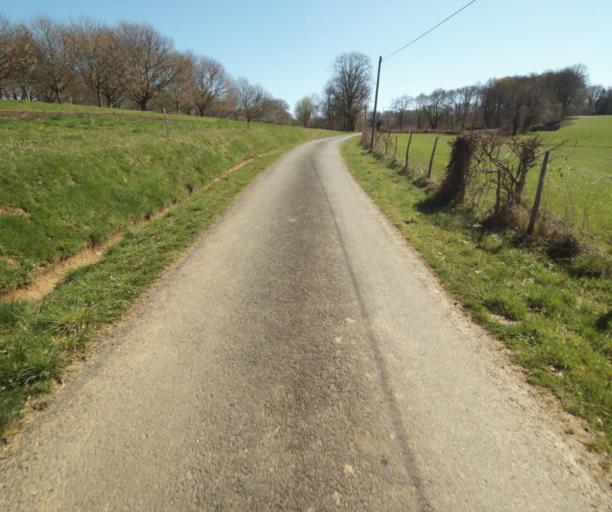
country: FR
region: Limousin
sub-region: Departement de la Correze
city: Saint-Clement
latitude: 45.3913
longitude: 1.6498
